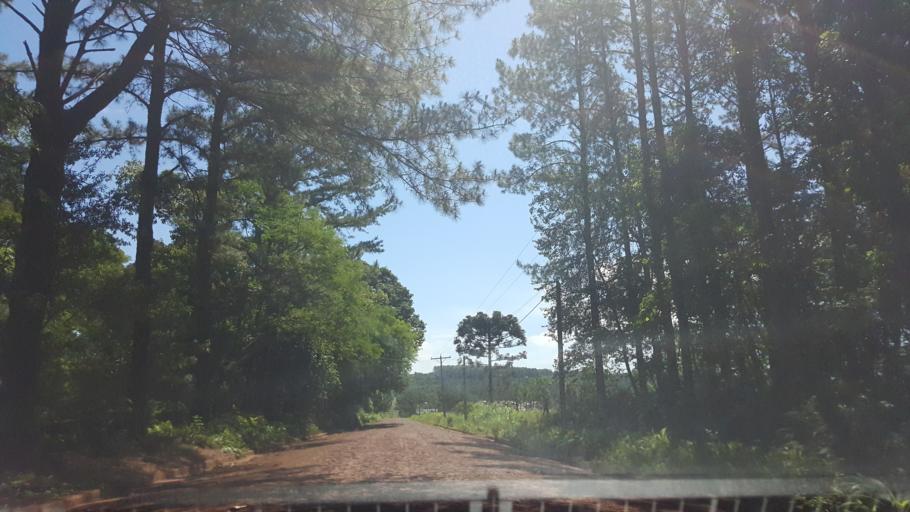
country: AR
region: Misiones
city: Capiovi
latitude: -26.9318
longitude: -55.0680
